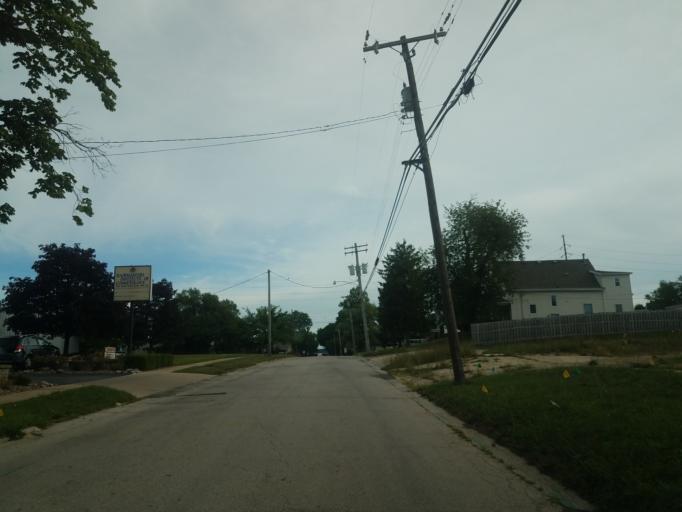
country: US
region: Illinois
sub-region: McLean County
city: Bloomington
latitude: 40.4752
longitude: -88.9800
